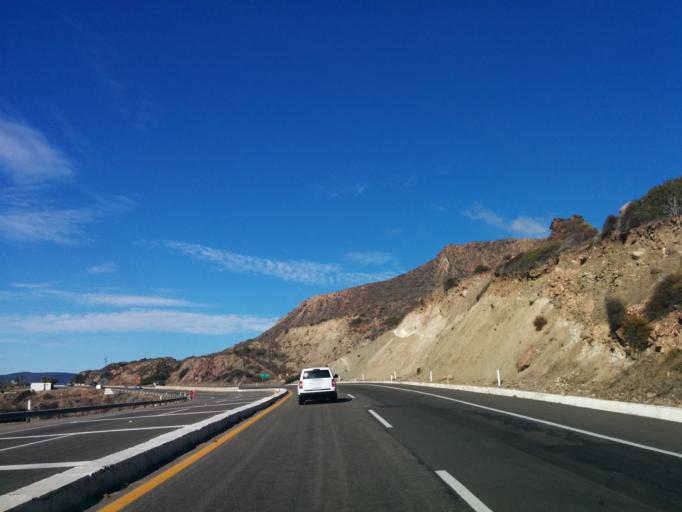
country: MX
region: Baja California
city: El Sauzal
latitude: 31.9279
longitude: -116.7523
